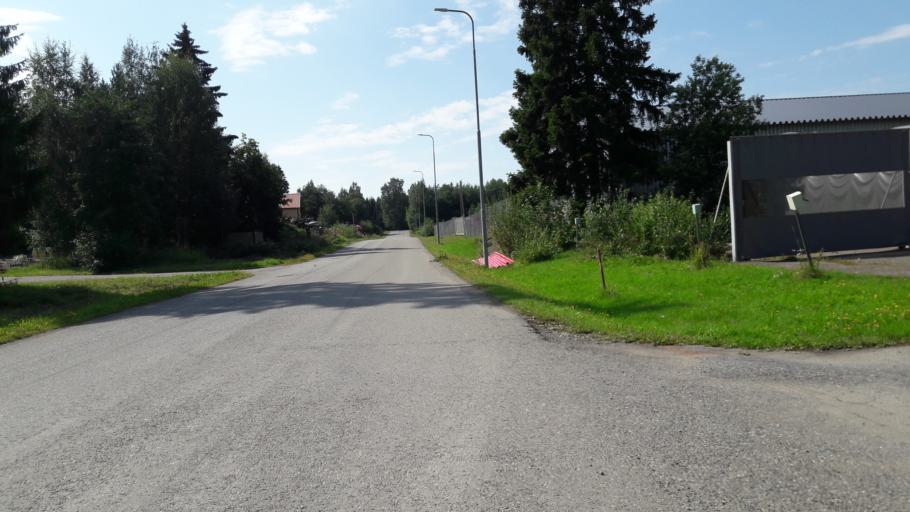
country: FI
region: North Karelia
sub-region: Joensuu
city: Joensuu
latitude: 62.5509
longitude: 29.8321
